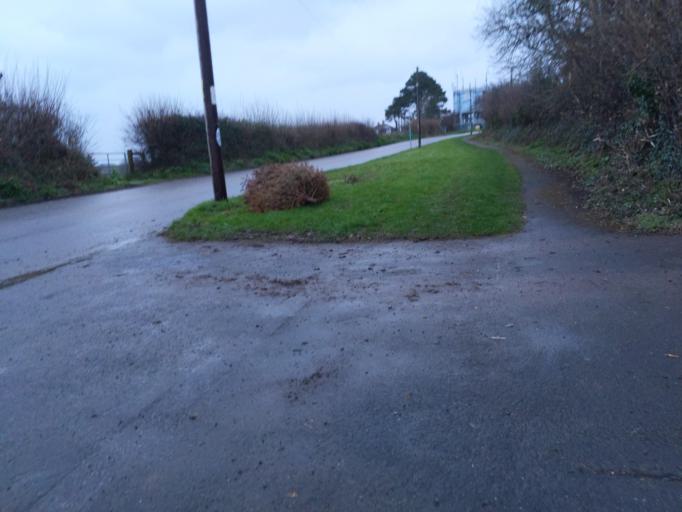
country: GB
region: England
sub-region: Devon
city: Wembury
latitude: 50.3212
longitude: -4.0337
